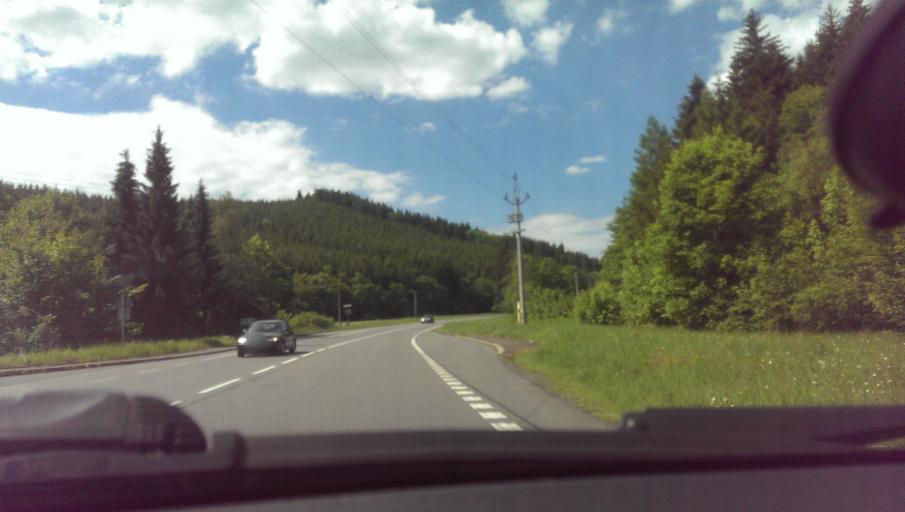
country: CZ
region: Zlin
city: Valasska Polanka
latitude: 49.2449
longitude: 17.9858
